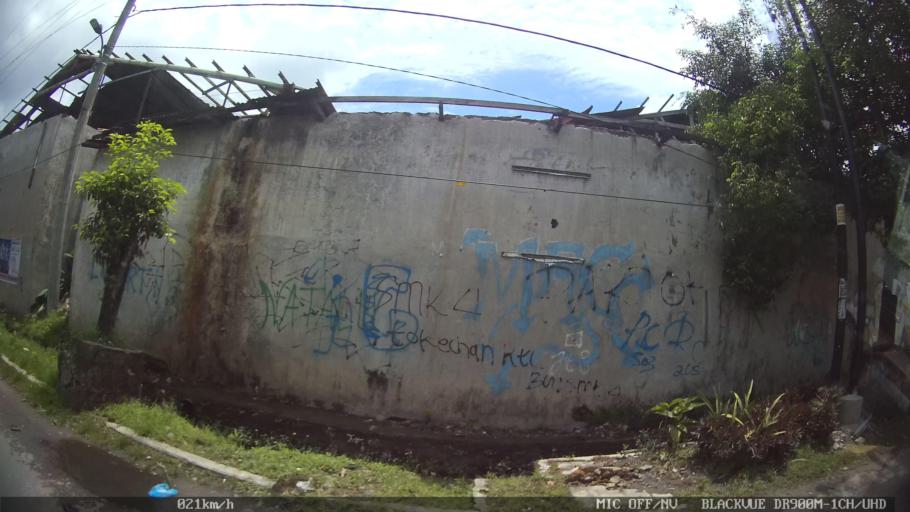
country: ID
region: North Sumatra
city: Medan
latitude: 3.5981
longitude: 98.7285
